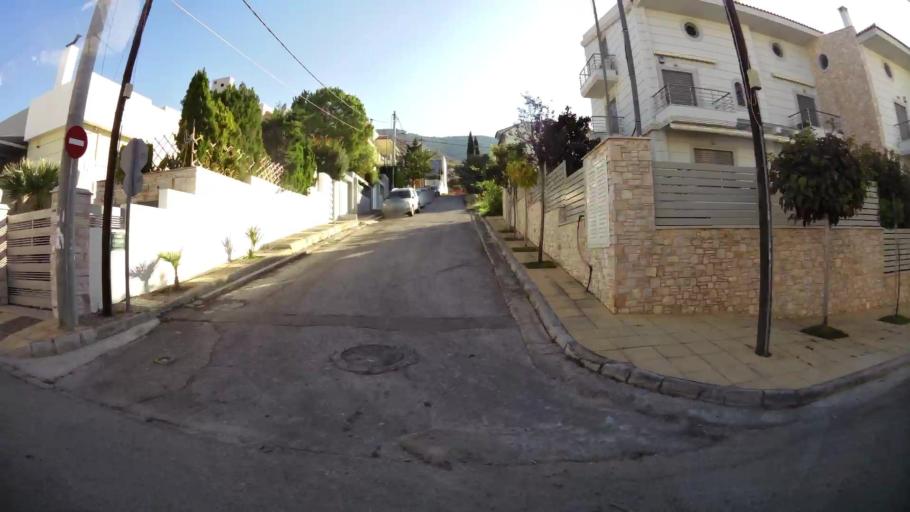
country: GR
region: Attica
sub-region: Nomarchia Athinas
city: Glyfada
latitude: 37.8753
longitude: 23.7716
